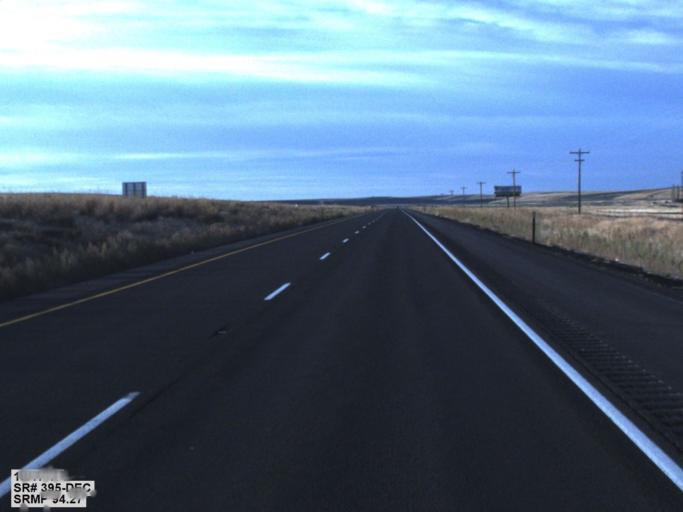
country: US
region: Washington
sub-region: Adams County
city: Ritzville
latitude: 47.0923
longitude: -118.4100
